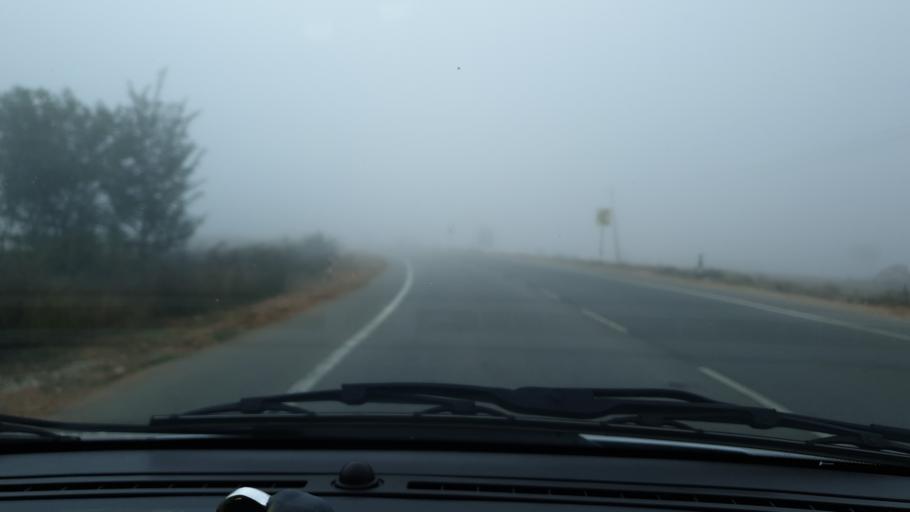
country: IN
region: Telangana
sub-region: Mahbubnagar
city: Nagar Karnul
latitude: 16.6667
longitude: 78.5301
